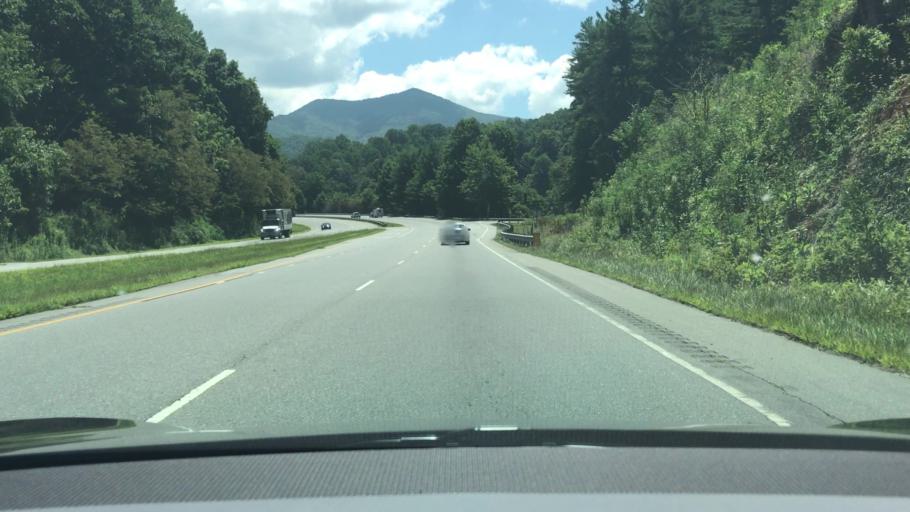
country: US
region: North Carolina
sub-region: Jackson County
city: Sylva
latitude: 35.3932
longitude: -83.1497
